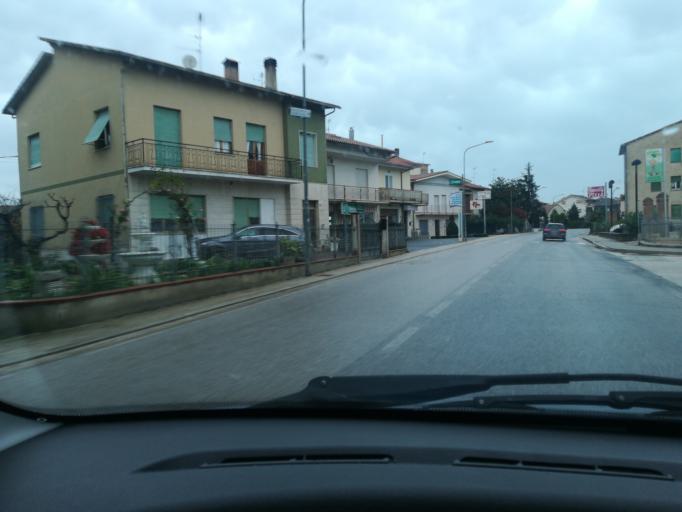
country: IT
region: The Marches
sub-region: Provincia di Macerata
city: Borgo Stazione
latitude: 43.2849
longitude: 13.6433
